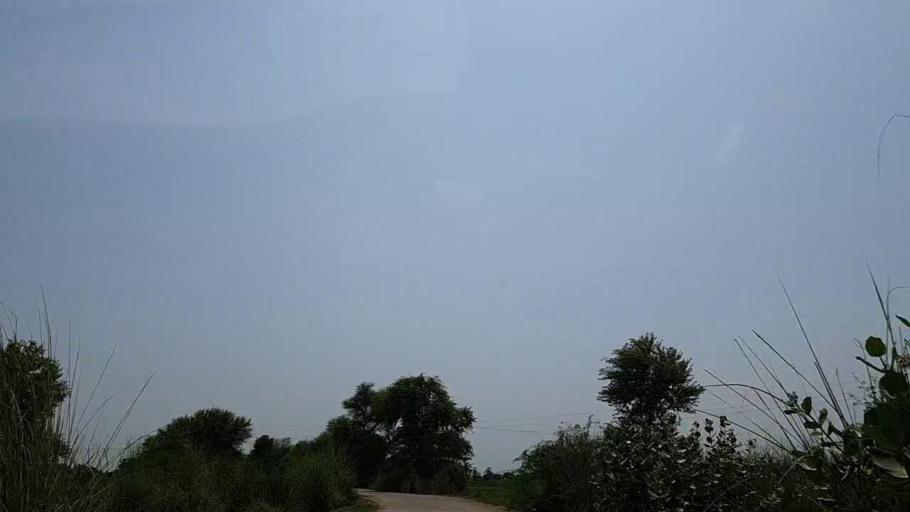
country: PK
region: Sindh
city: Adilpur
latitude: 27.9117
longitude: 69.3665
